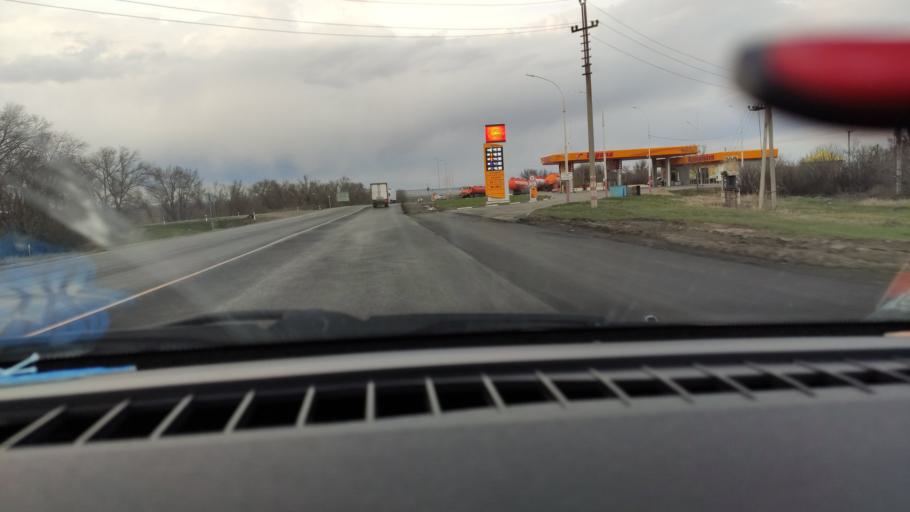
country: RU
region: Saratov
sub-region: Saratovskiy Rayon
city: Saratov
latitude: 51.6853
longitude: 46.0032
